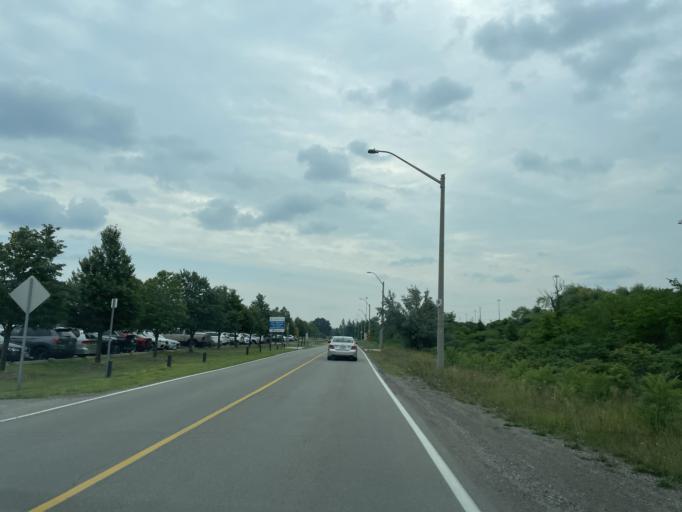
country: CA
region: Ontario
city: Hamilton
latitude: 43.2622
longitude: -79.7696
